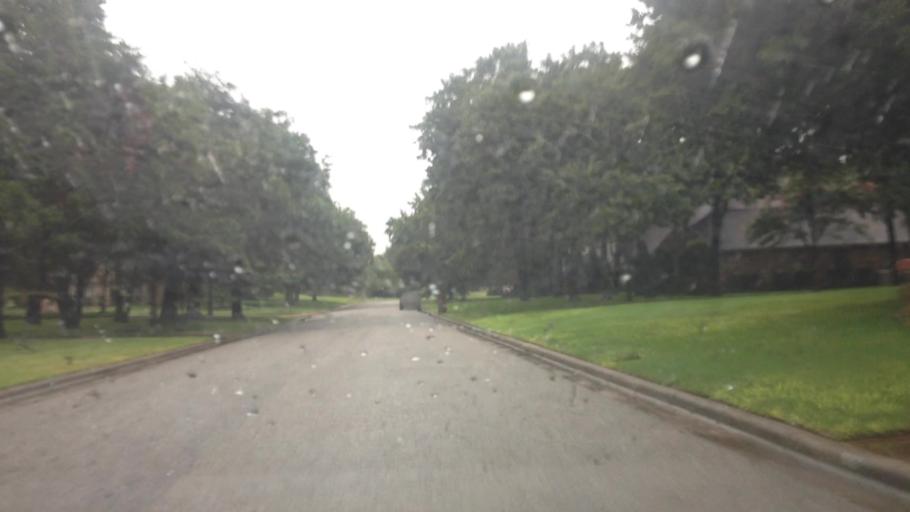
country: US
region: Texas
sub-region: Denton County
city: Trophy Club
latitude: 32.9535
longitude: -97.1966
